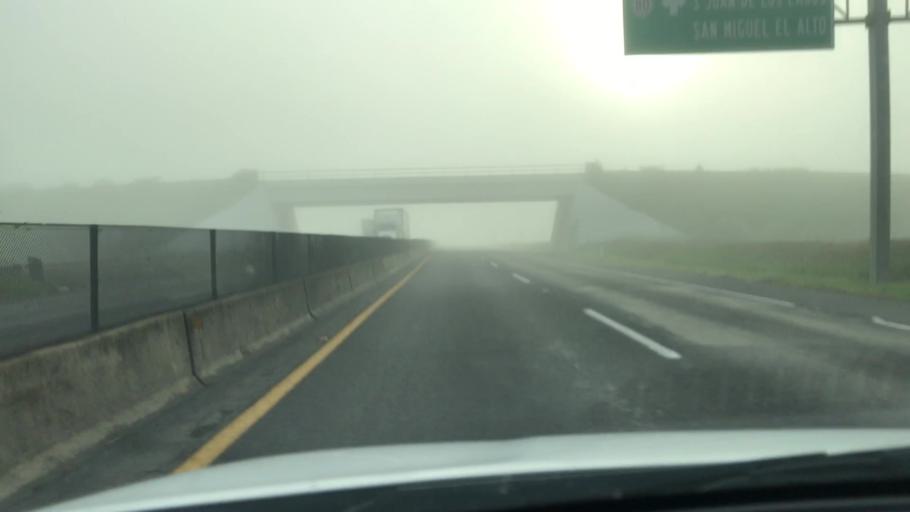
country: MX
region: Jalisco
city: Tepatitlan de Morelos
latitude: 20.8907
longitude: -102.7151
